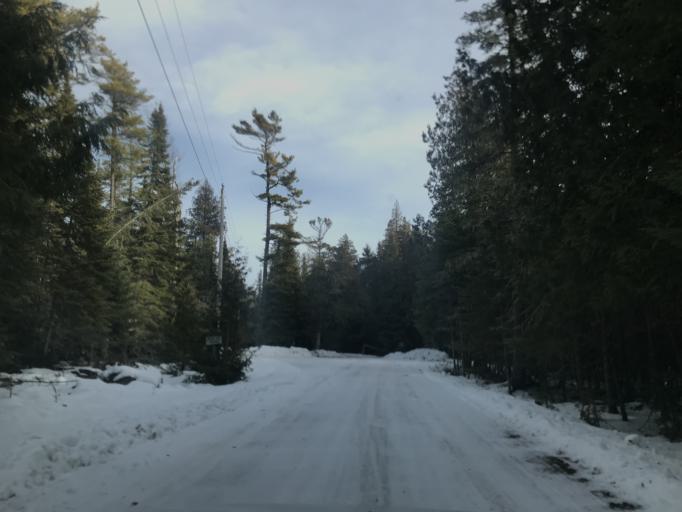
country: US
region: Wisconsin
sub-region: Door County
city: Sturgeon Bay
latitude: 45.1418
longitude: -87.0388
